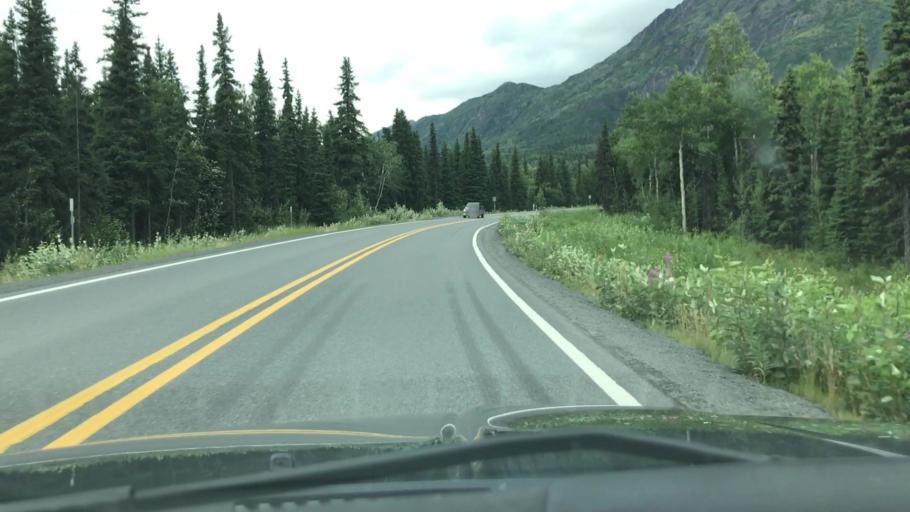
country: US
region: Alaska
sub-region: Kenai Peninsula Borough
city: Seward
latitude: 60.4837
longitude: -149.9571
